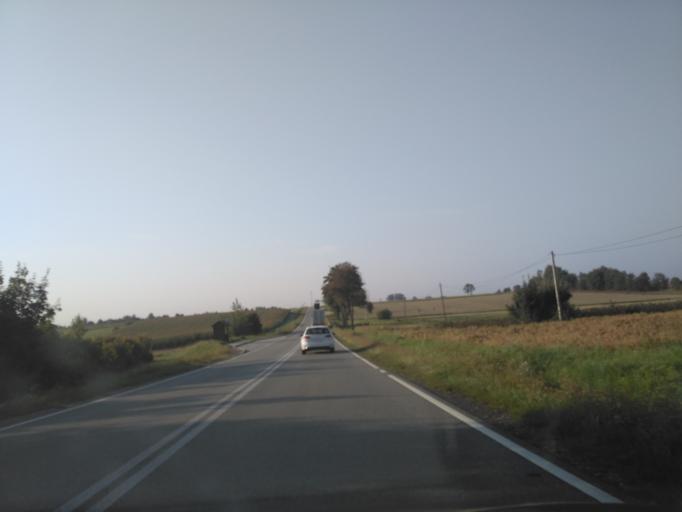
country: PL
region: Lublin Voivodeship
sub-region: Powiat janowski
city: Modliborzyce
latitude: 50.7823
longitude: 22.3233
